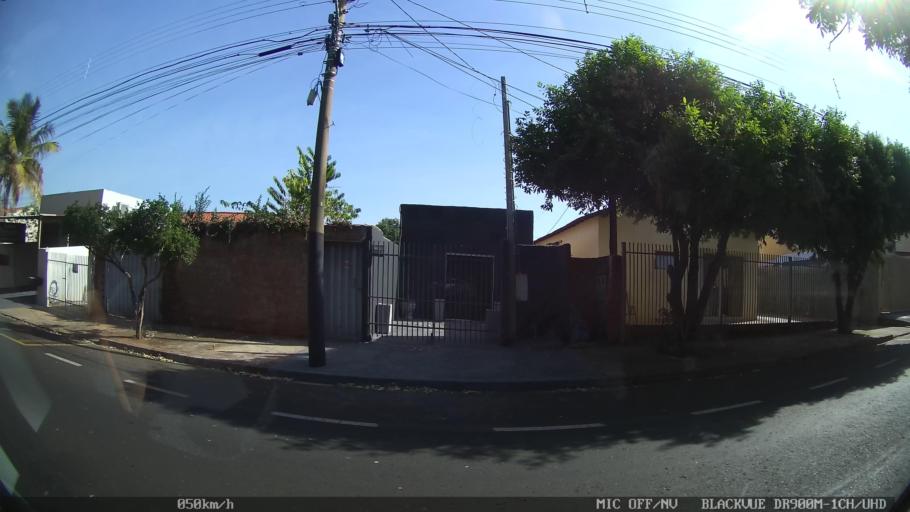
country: BR
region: Sao Paulo
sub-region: Sao Jose Do Rio Preto
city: Sao Jose do Rio Preto
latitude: -20.7988
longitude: -49.4172
